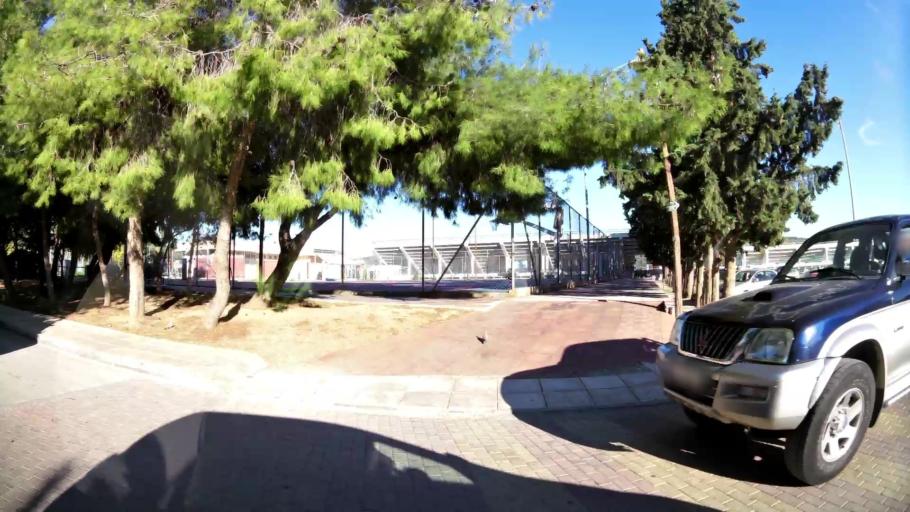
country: GR
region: Attica
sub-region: Nomarchia Anatolikis Attikis
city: Vari
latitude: 37.8308
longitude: 23.8055
